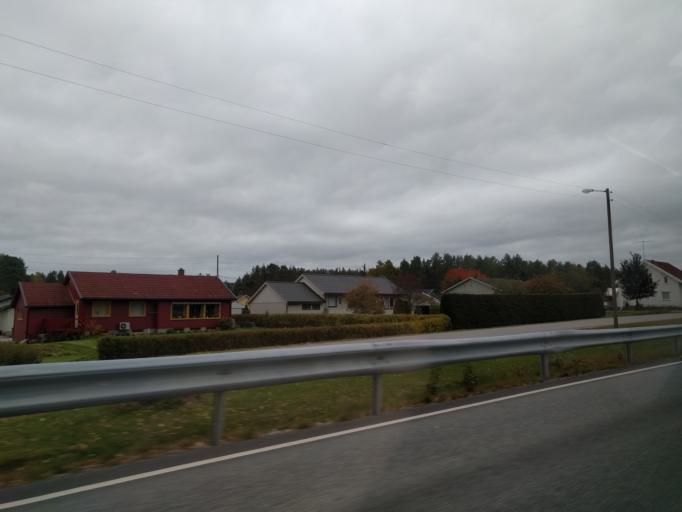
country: NO
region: Aust-Agder
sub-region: Evje og Hornnes
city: Evje
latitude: 58.5847
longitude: 7.8016
